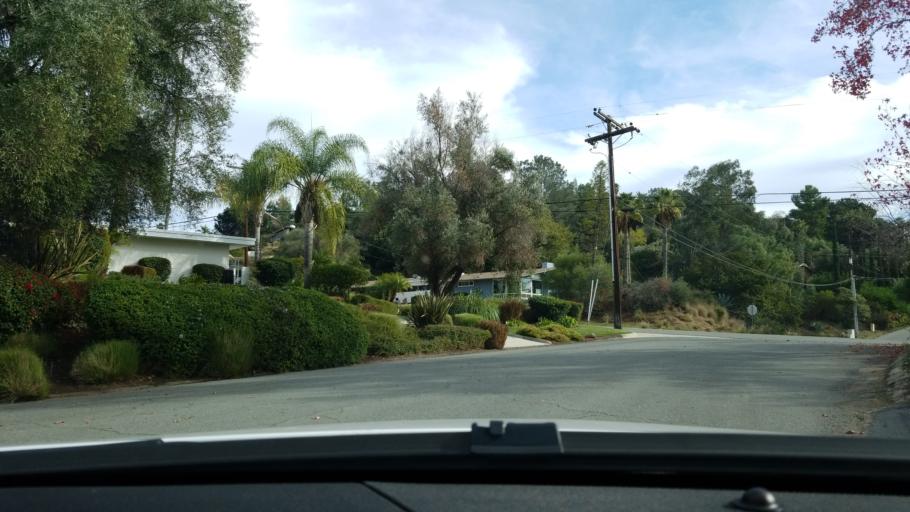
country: US
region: California
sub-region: San Diego County
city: Casa de Oro-Mount Helix
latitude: 32.7717
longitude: -116.9544
